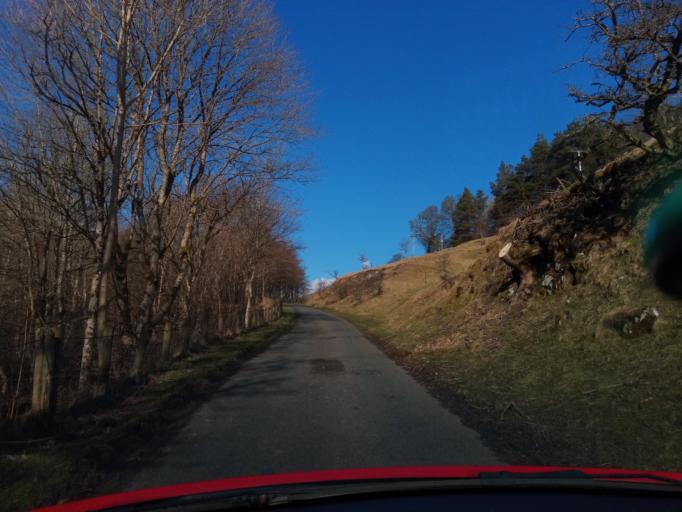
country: GB
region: Scotland
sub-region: The Scottish Borders
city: Hawick
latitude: 55.4231
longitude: -2.8722
